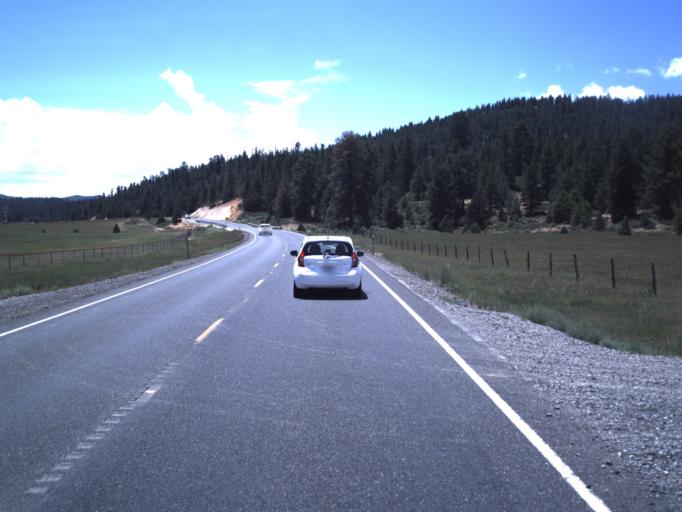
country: US
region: Utah
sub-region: Garfield County
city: Panguitch
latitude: 37.4452
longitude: -112.5364
